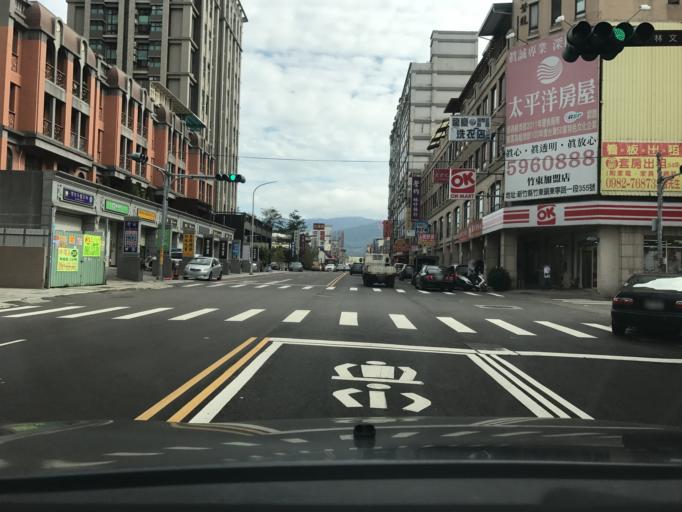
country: TW
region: Taiwan
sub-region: Hsinchu
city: Zhubei
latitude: 24.7364
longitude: 121.0957
